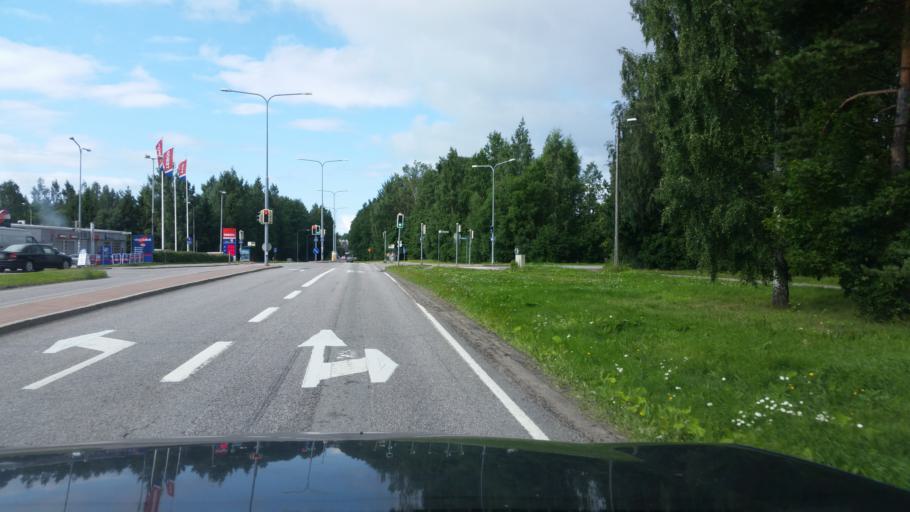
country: FI
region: Uusimaa
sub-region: Helsinki
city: Vantaa
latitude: 60.2243
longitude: 25.1156
